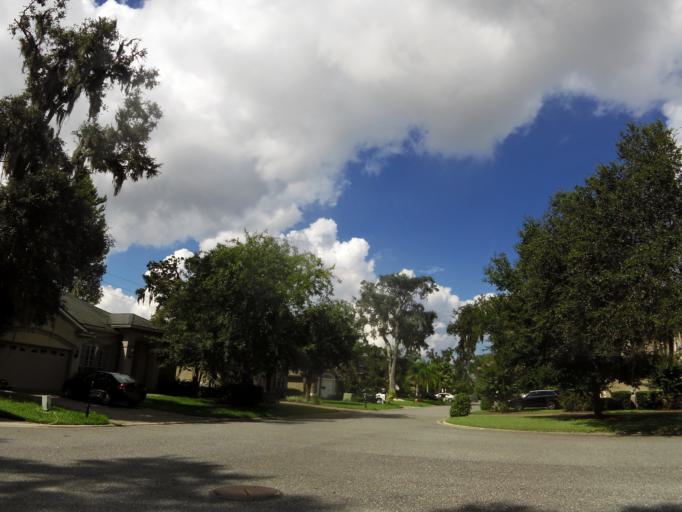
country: US
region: Florida
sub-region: Nassau County
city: Fernandina Beach
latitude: 30.6239
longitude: -81.4601
